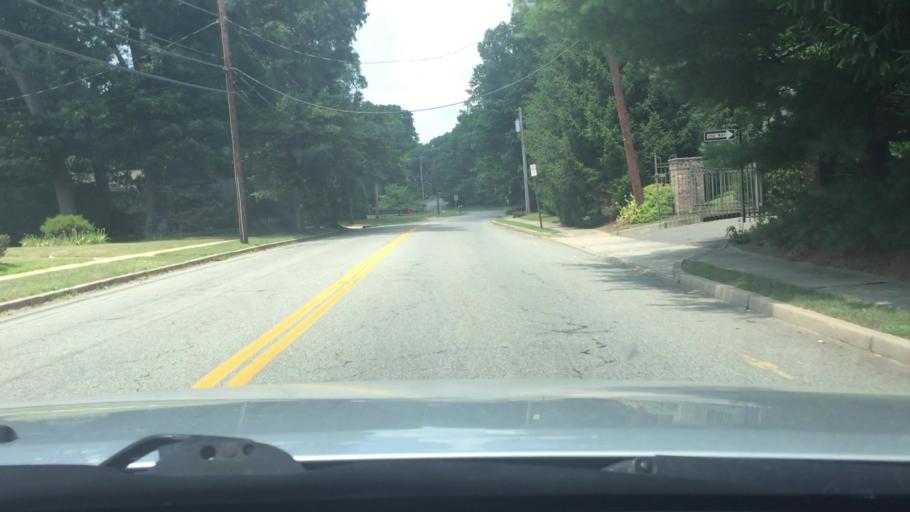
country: US
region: New Jersey
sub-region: Middlesex County
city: Spotswood
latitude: 40.4062
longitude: -74.4048
